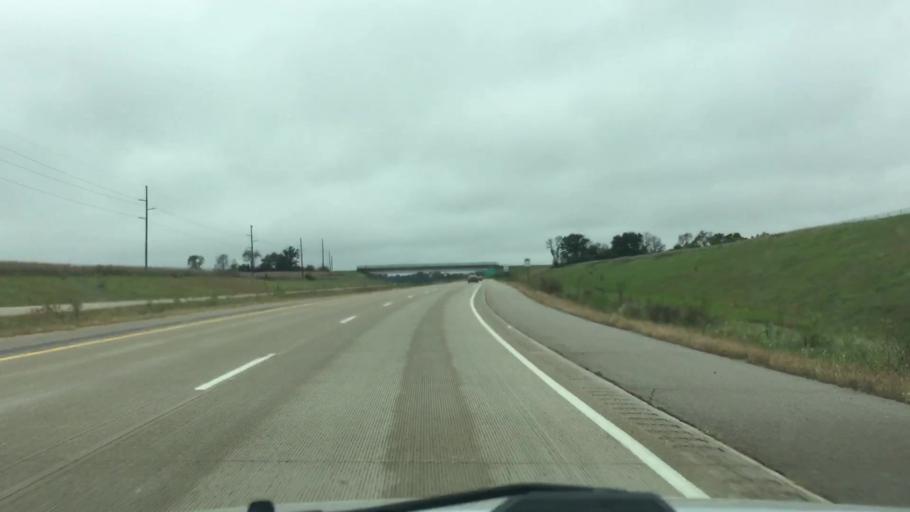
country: US
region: Wisconsin
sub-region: Rock County
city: Milton
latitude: 42.7624
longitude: -88.9306
